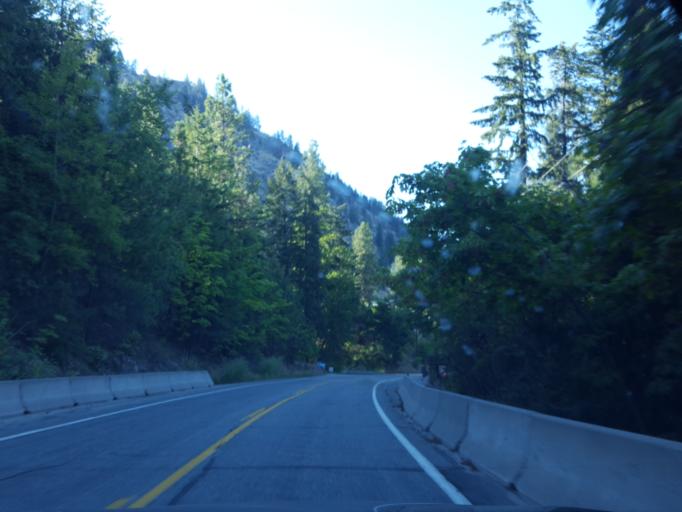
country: US
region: Washington
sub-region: Chelan County
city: Granite Falls
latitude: 47.8890
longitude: -120.2143
